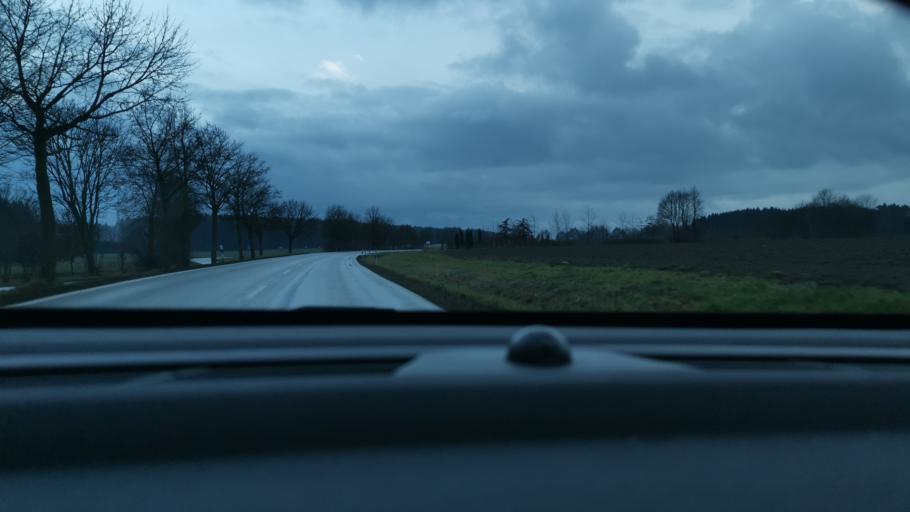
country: DE
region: Bavaria
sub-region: Swabia
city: Petersdorf
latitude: 48.5026
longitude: 11.0163
